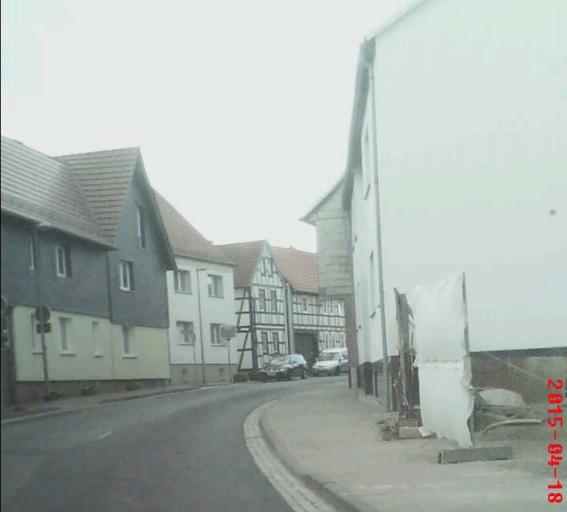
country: DE
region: Thuringia
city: Hausen
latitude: 51.3856
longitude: 10.3594
